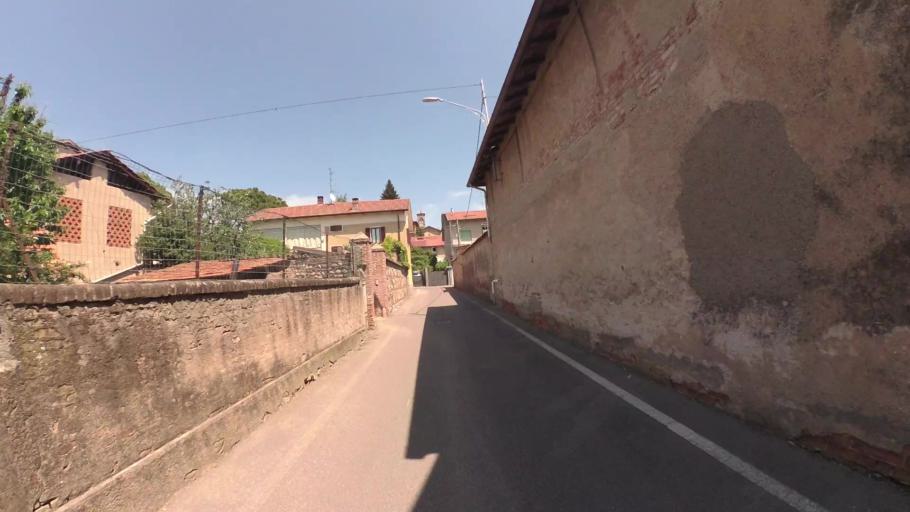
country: IT
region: Lombardy
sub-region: Provincia di Varese
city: Tradate
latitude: 45.7160
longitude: 8.9053
